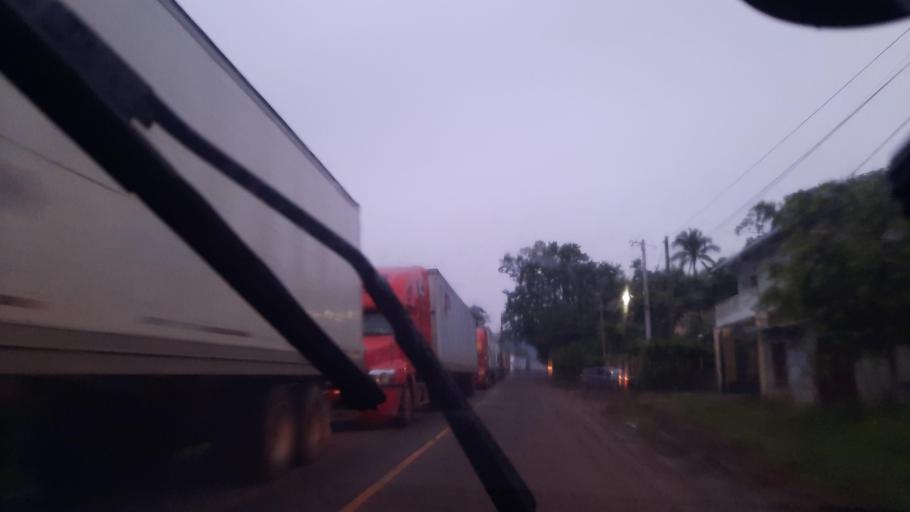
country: GT
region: Jutiapa
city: Atescatempa
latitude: 14.2017
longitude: -89.6798
